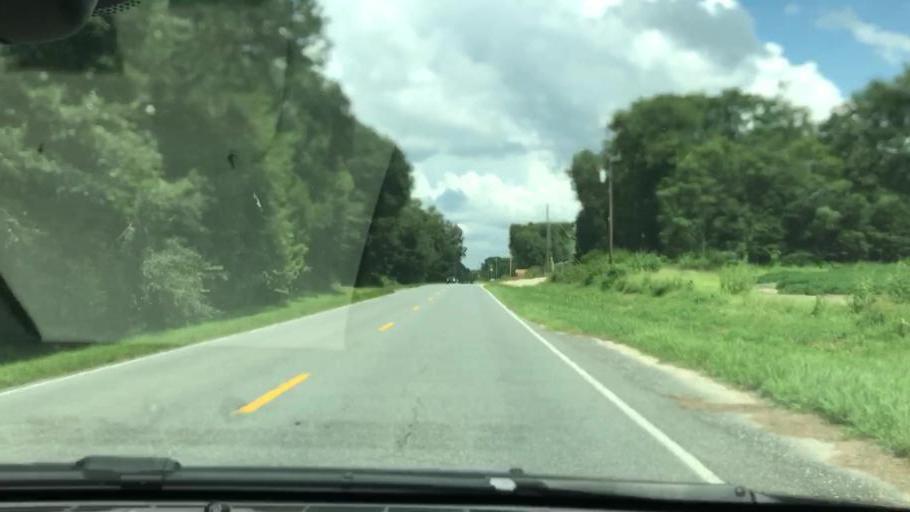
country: US
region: Florida
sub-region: Jackson County
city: Malone
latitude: 30.9014
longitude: -85.1332
